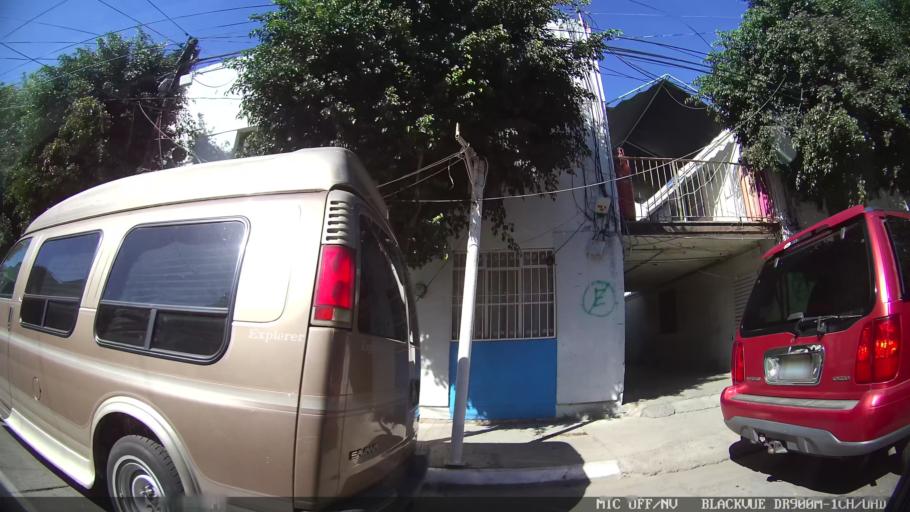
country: MX
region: Jalisco
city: Tlaquepaque
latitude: 20.6736
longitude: -103.2853
